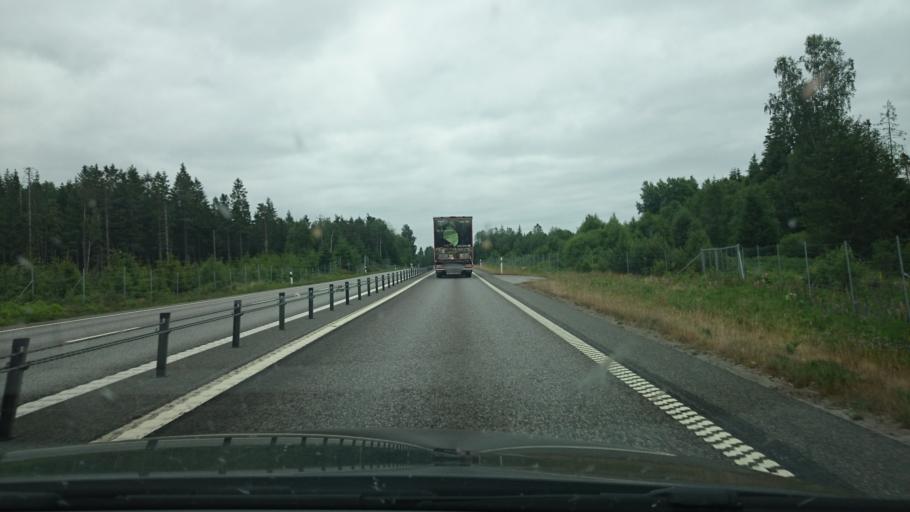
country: SE
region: Halland
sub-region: Hylte Kommun
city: Hyltebruk
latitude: 56.9773
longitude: 13.1886
